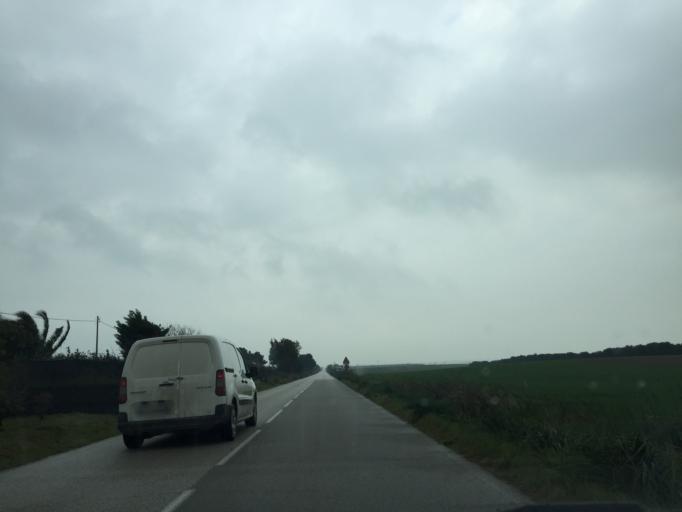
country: IT
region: Apulia
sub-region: Provincia di Foggia
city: Castelluccio dei Sauri
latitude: 41.4109
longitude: 15.4506
